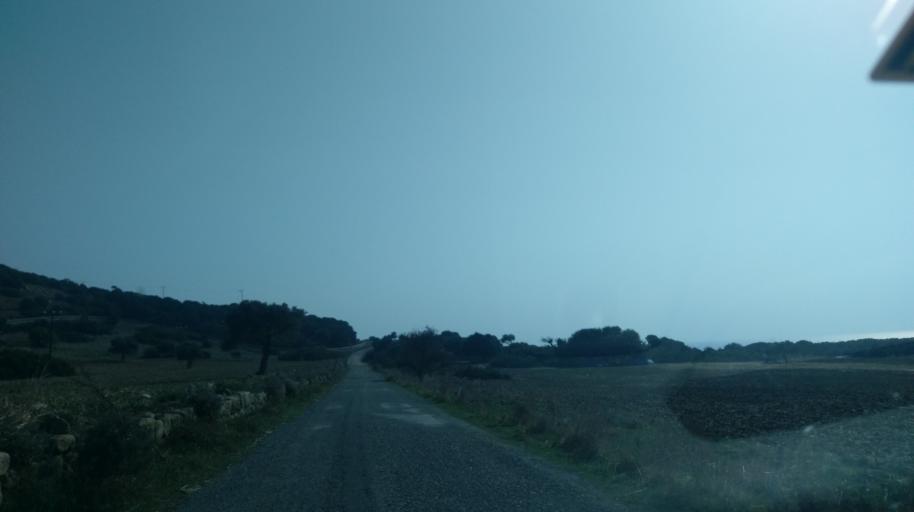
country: CY
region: Ammochostos
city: Rizokarpaso
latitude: 35.6479
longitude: 34.5526
